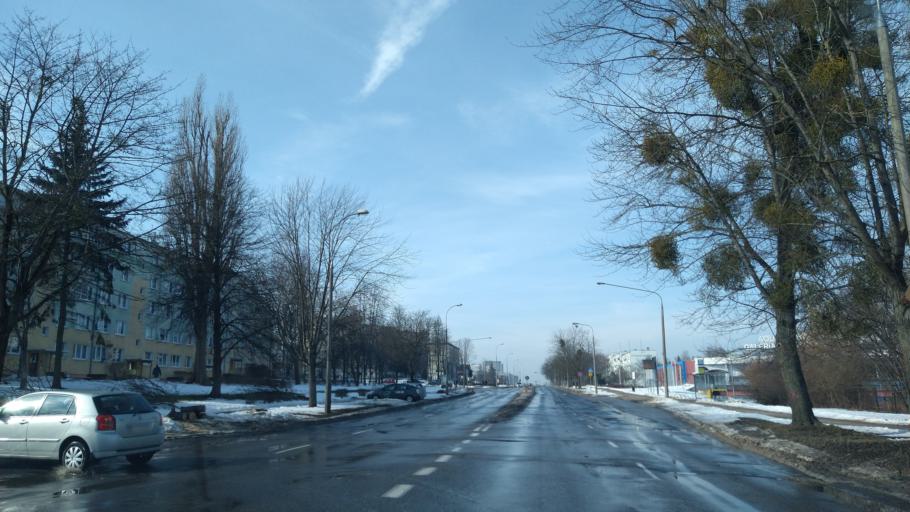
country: PL
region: Warmian-Masurian Voivodeship
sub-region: Powiat olsztynski
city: Olsztyn
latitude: 53.7711
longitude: 20.5076
